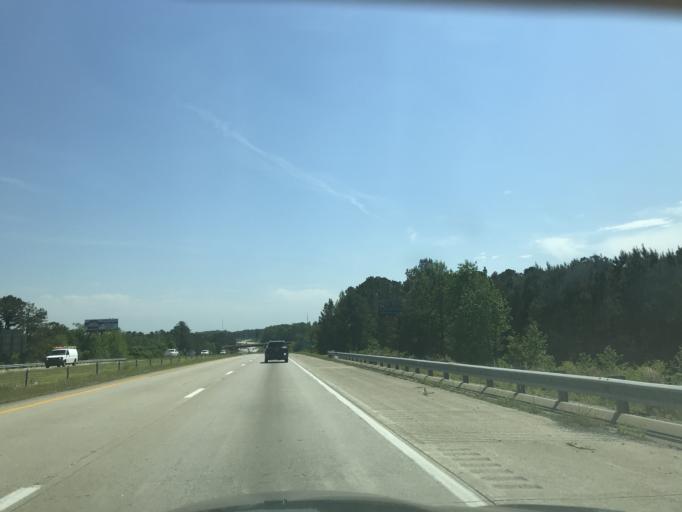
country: US
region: North Carolina
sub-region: Johnston County
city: Benson
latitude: 35.4034
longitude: -78.5235
